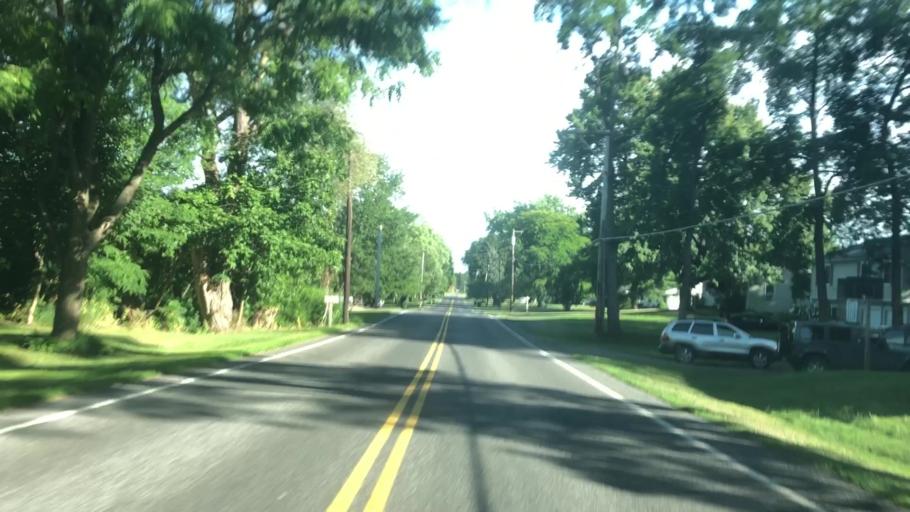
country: US
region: New York
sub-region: Wayne County
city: Macedon
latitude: 43.1199
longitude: -77.3059
